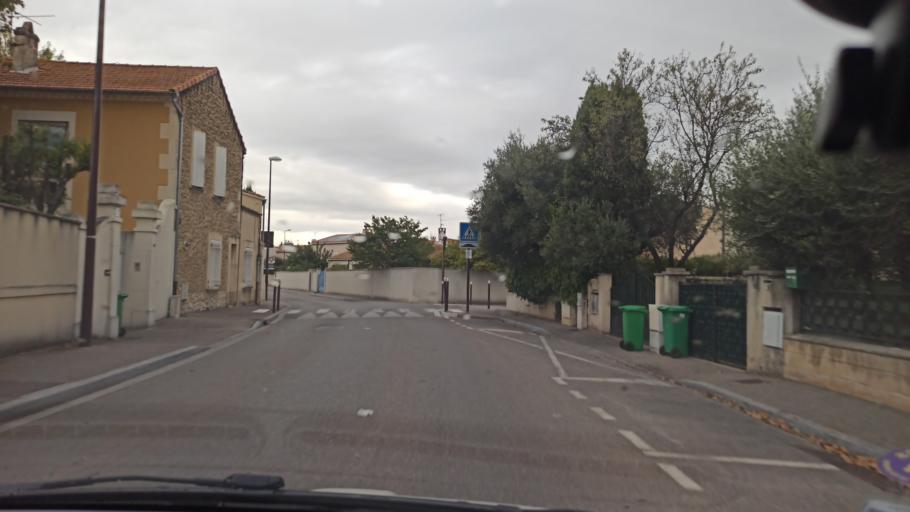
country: FR
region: Provence-Alpes-Cote d'Azur
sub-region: Departement du Vaucluse
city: Montfavet
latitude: 43.9388
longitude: 4.8775
